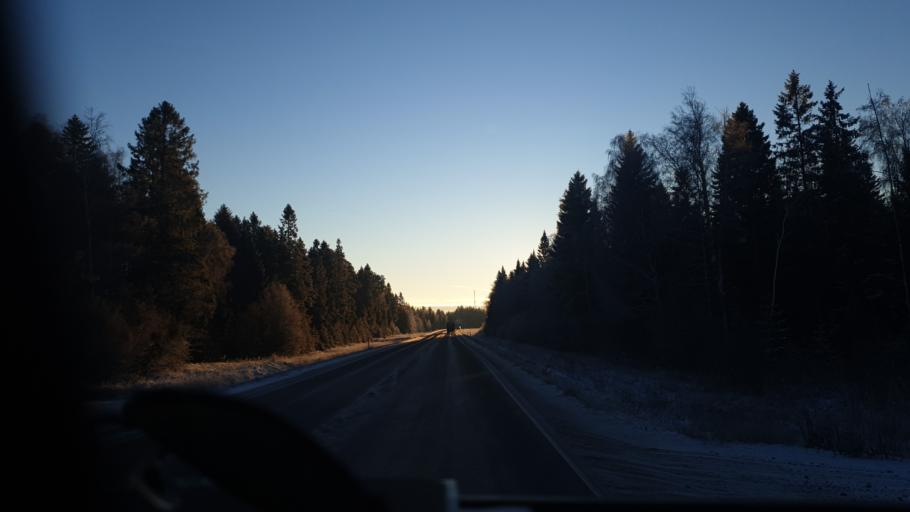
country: FI
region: Northern Ostrobothnia
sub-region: Ylivieska
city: Kalajoki
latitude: 64.2940
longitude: 23.9413
